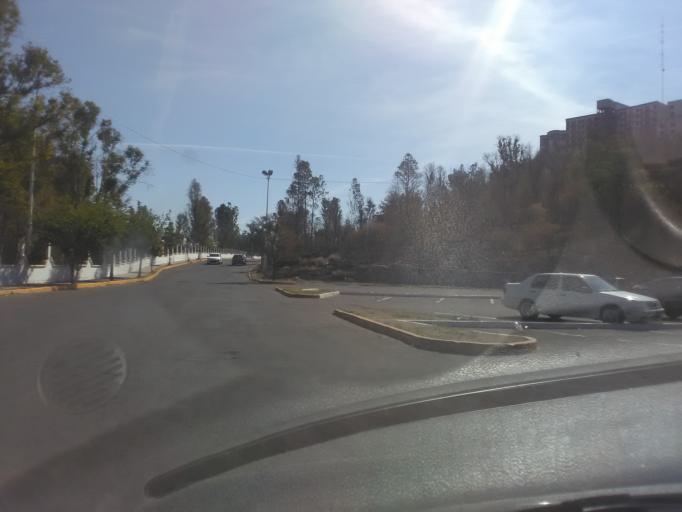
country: MX
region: Durango
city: Victoria de Durango
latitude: 24.0236
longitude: -104.6859
